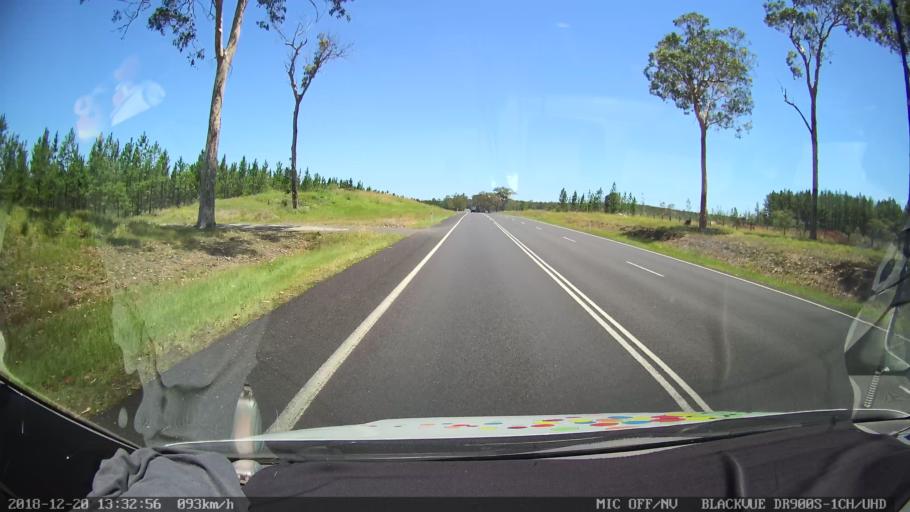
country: AU
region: New South Wales
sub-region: Clarence Valley
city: Gordon
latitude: -29.2386
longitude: 152.9884
